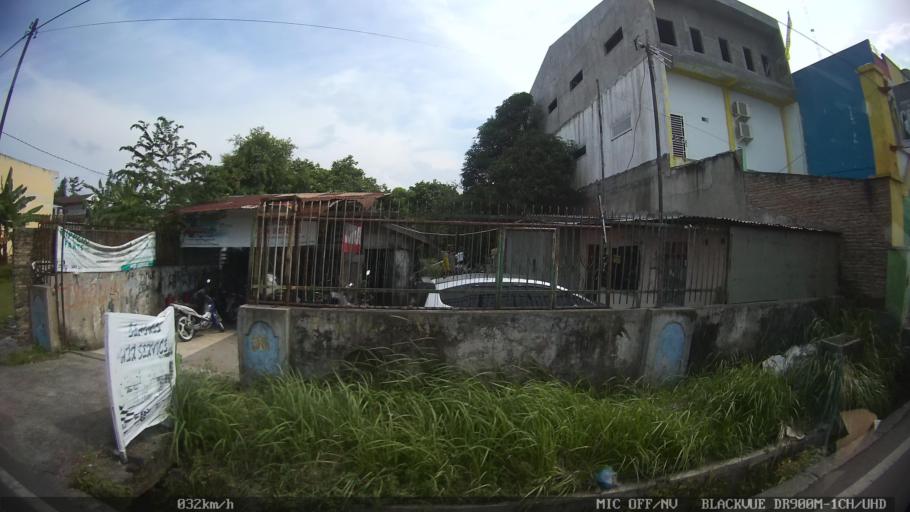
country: ID
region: North Sumatra
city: Percut
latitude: 3.6071
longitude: 98.7666
